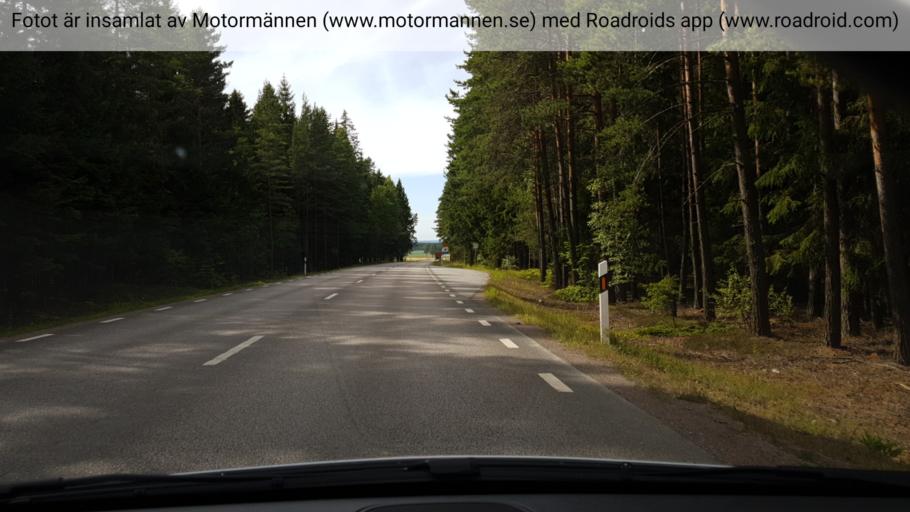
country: SE
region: Vaestra Goetaland
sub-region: Tibro Kommun
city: Tibro
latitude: 58.3436
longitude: 14.1558
